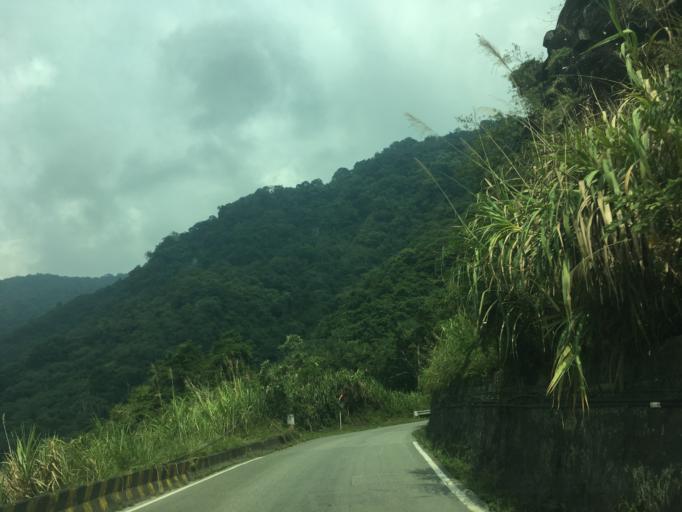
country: TW
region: Taiwan
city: Fengyuan
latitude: 24.3425
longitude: 120.9382
